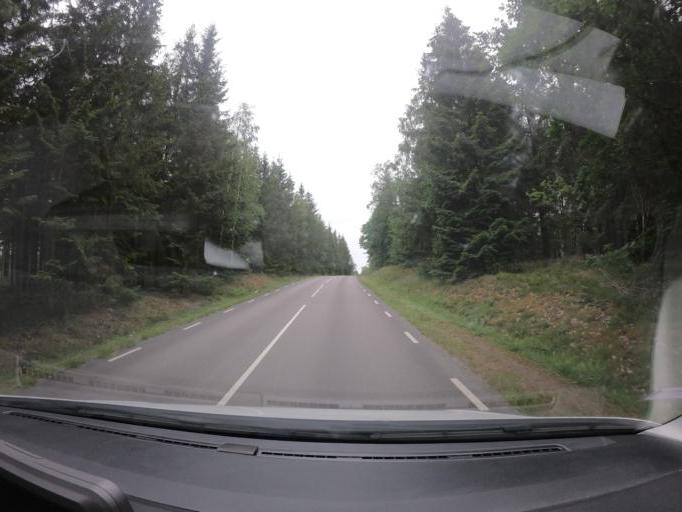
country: SE
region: Skane
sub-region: Perstorps Kommun
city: Perstorp
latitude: 56.1033
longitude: 13.4126
